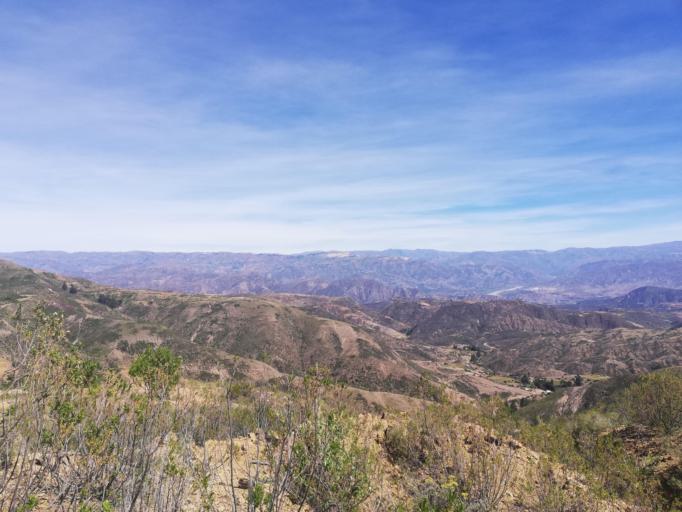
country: BO
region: Cochabamba
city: Capinota
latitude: -17.6370
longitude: -66.2618
